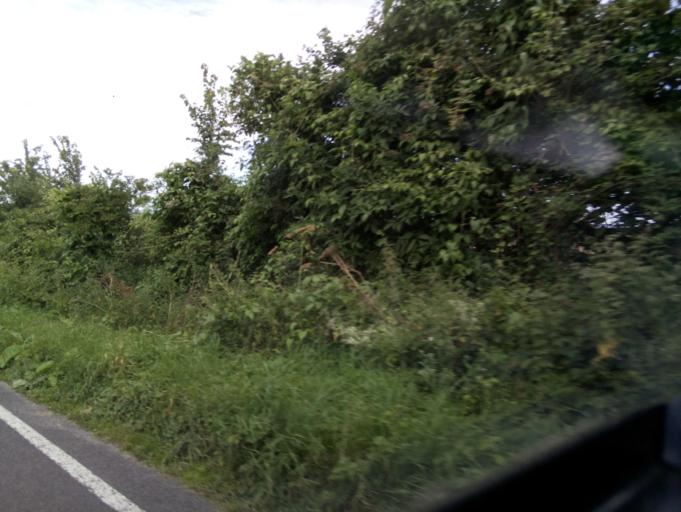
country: GB
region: England
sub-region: Somerset
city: Street
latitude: 51.0904
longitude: -2.6908
